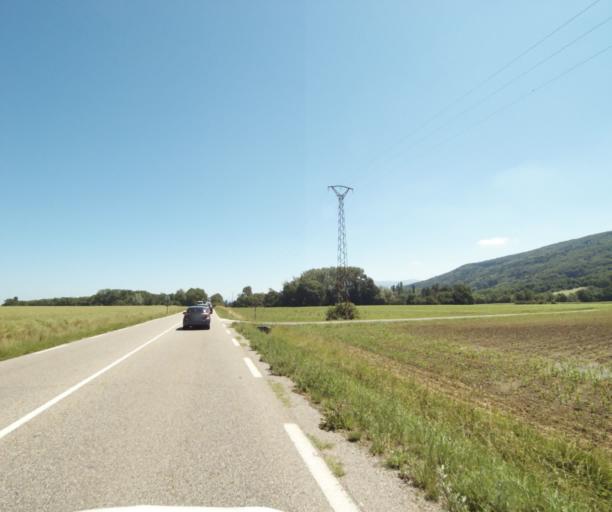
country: FR
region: Rhone-Alpes
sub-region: Departement de la Haute-Savoie
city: Massongy
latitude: 46.3205
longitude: 6.3372
